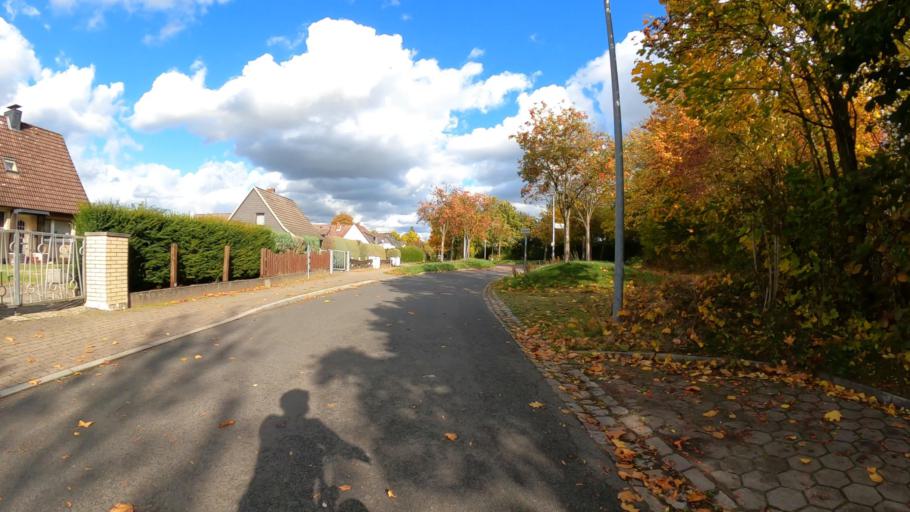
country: DE
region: Schleswig-Holstein
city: Ahrensburg
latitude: 53.6794
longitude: 10.2292
